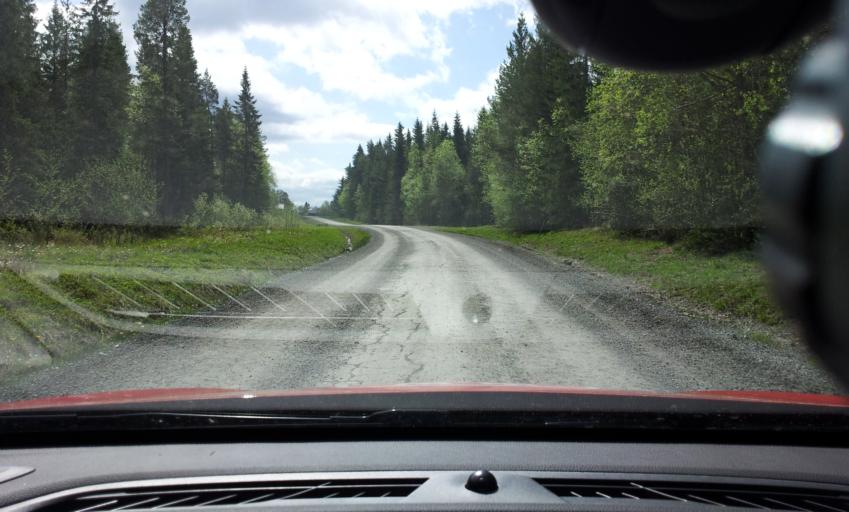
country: SE
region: Jaemtland
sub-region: OEstersunds Kommun
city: Ostersund
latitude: 63.0621
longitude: 14.5533
